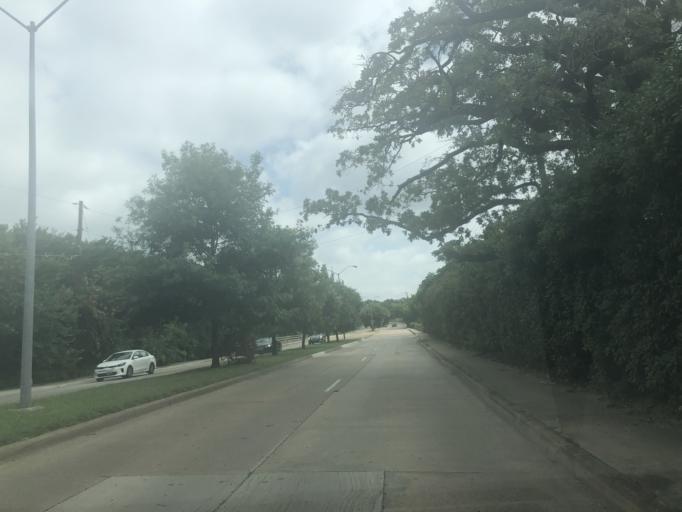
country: US
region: Texas
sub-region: Dallas County
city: University Park
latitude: 32.8595
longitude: -96.8372
